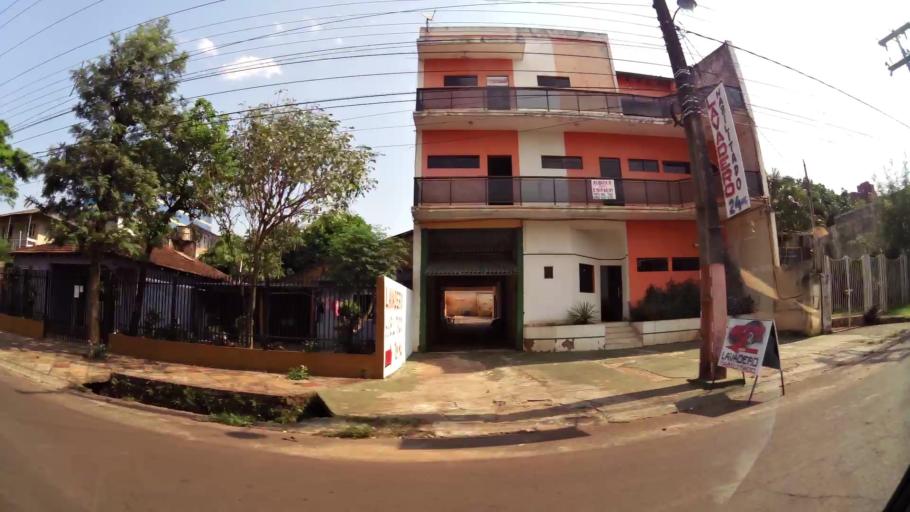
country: PY
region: Alto Parana
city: Ciudad del Este
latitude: -25.5087
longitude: -54.6287
